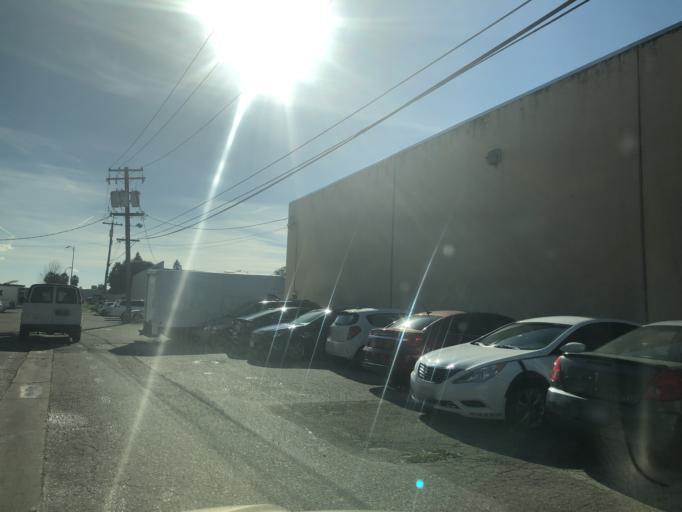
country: US
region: California
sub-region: Santa Clara County
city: Santa Clara
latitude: 37.3809
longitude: -121.9395
